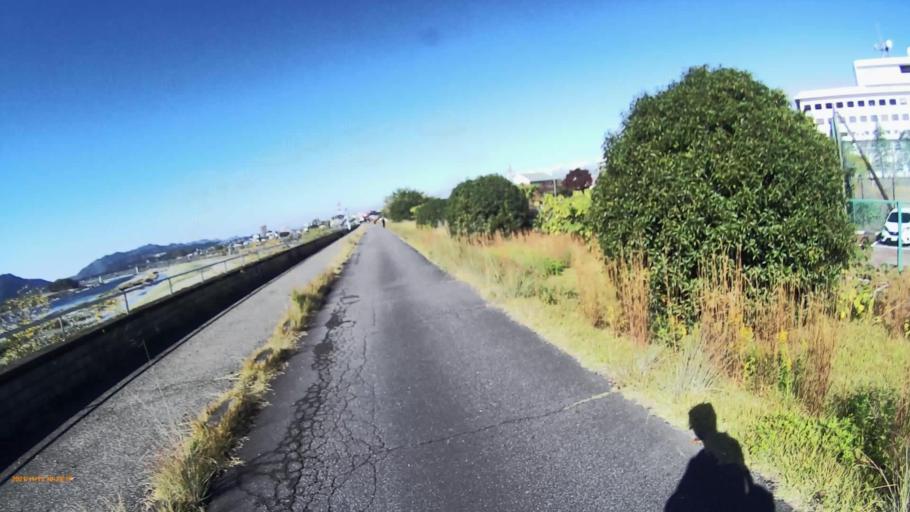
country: JP
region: Gifu
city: Minokamo
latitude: 35.4383
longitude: 137.0249
